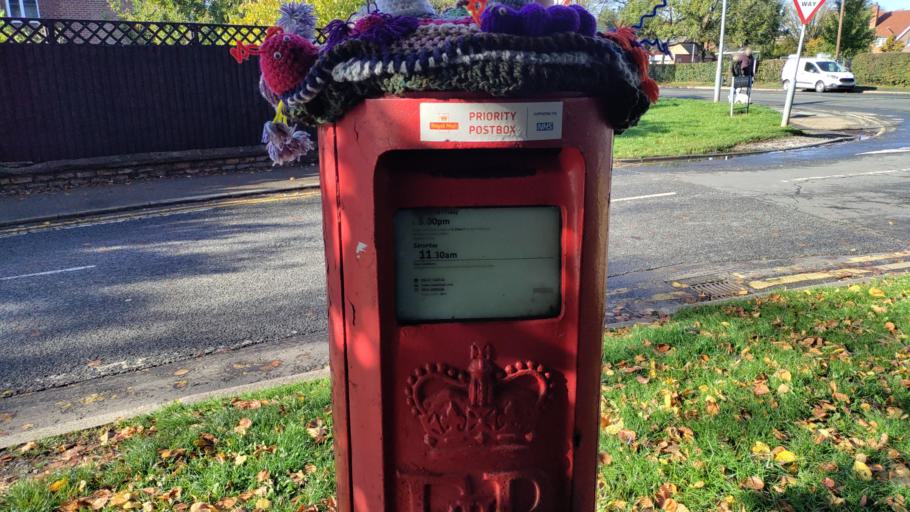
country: GB
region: England
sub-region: Cheshire West and Chester
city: Hartford
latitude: 53.2444
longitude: -2.5469
